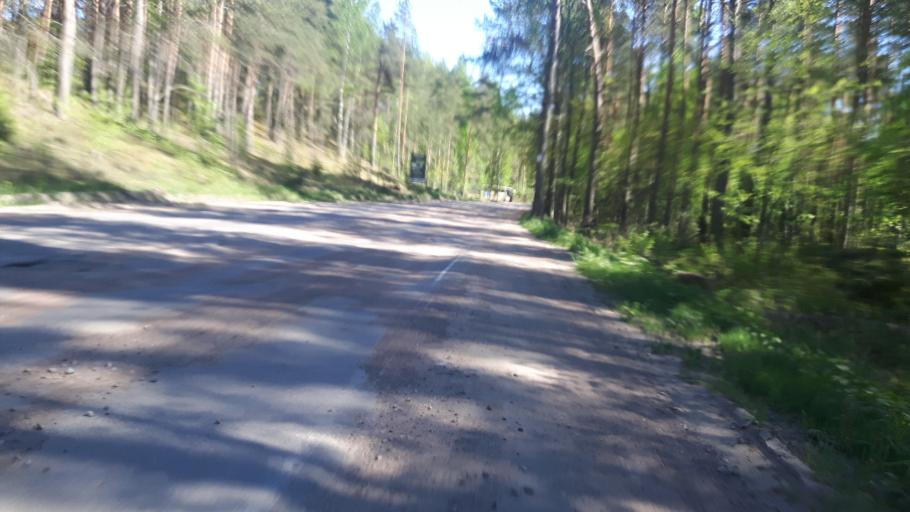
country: RU
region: Leningrad
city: Glebychevo
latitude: 60.2423
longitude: 28.9995
